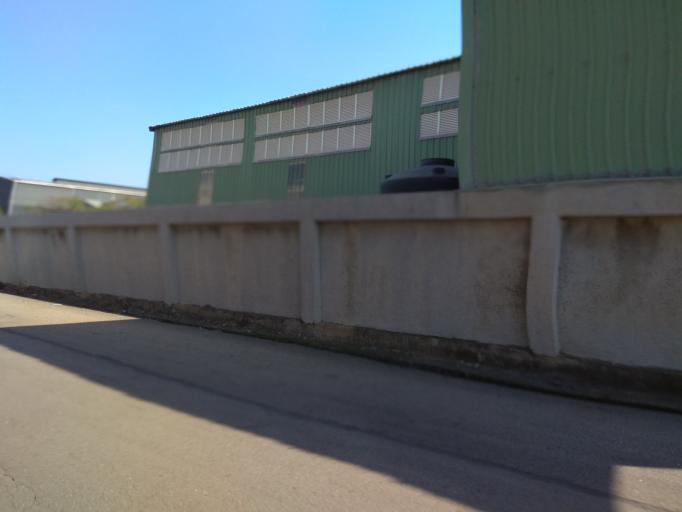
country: TW
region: Taiwan
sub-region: Hsinchu
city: Zhubei
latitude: 24.9831
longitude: 121.0356
